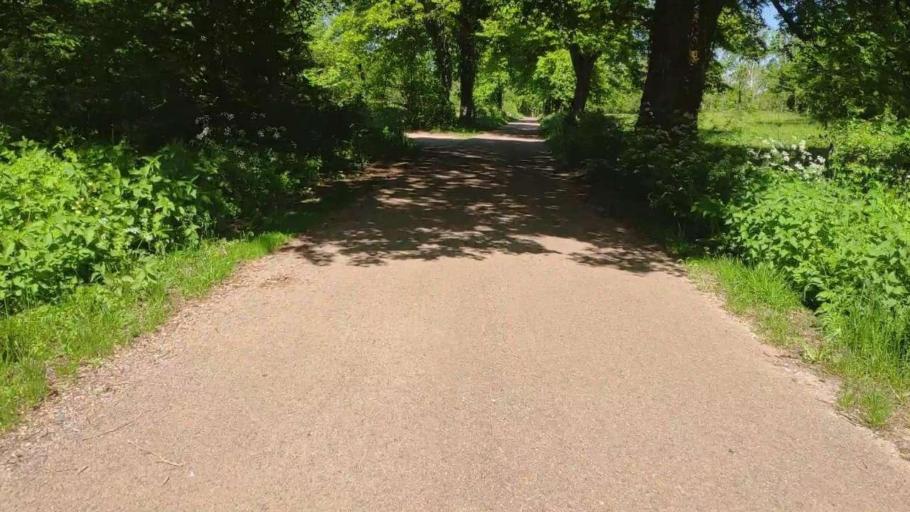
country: FR
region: Franche-Comte
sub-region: Departement du Jura
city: Poligny
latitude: 46.7318
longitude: 5.7363
